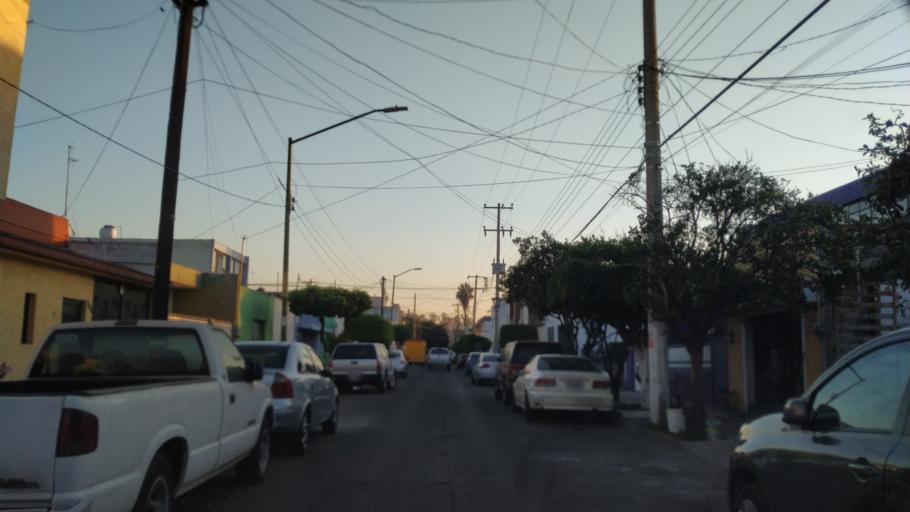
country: MX
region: Jalisco
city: Tlaquepaque
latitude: 20.6549
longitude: -103.3342
